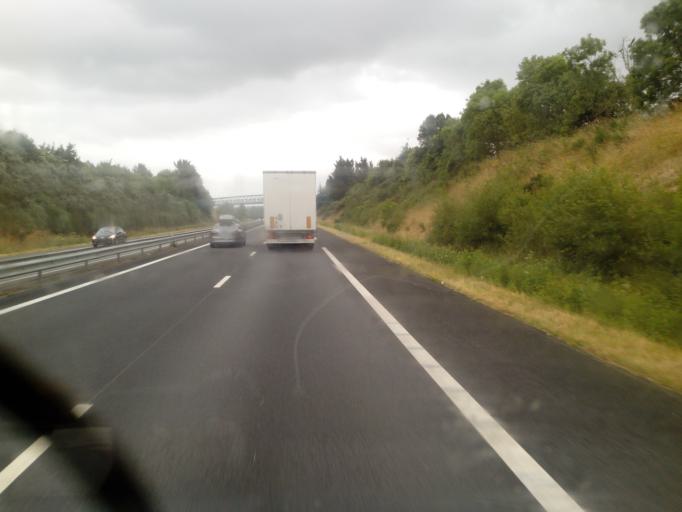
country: FR
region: Pays de la Loire
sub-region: Departement de la Loire-Atlantique
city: Derval
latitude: 47.6683
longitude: -1.6858
